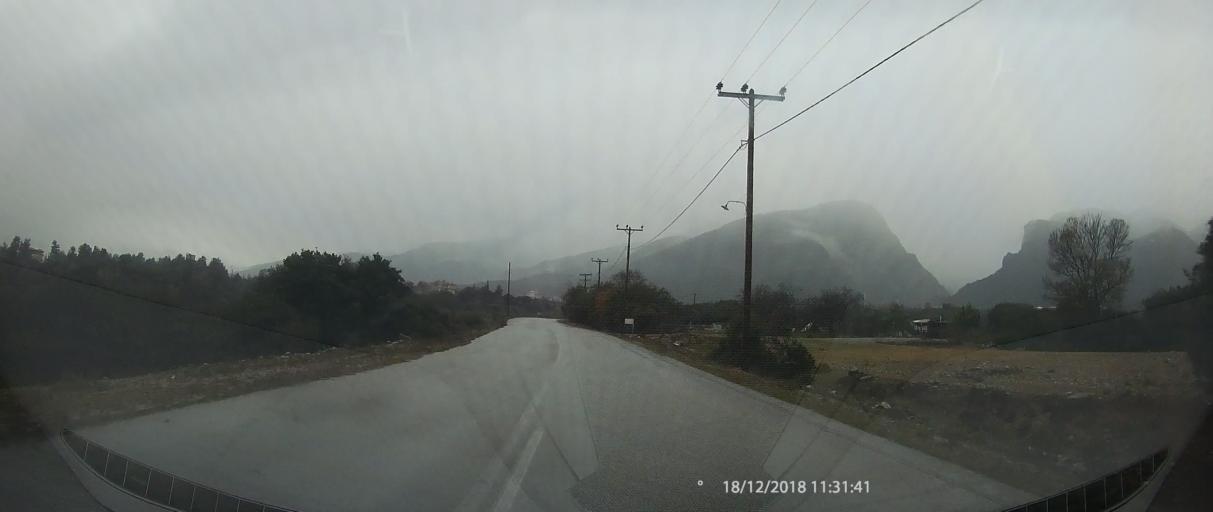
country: GR
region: Central Macedonia
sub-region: Nomos Pierias
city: Litochoro
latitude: 40.1121
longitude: 22.5077
